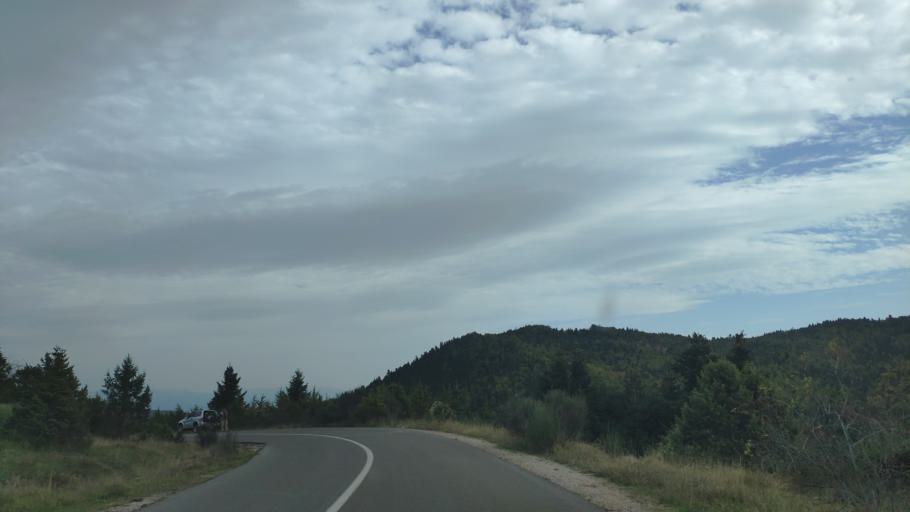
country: GR
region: Central Greece
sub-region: Nomos Fthiotidos
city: Stavros
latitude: 38.7142
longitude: 22.3259
